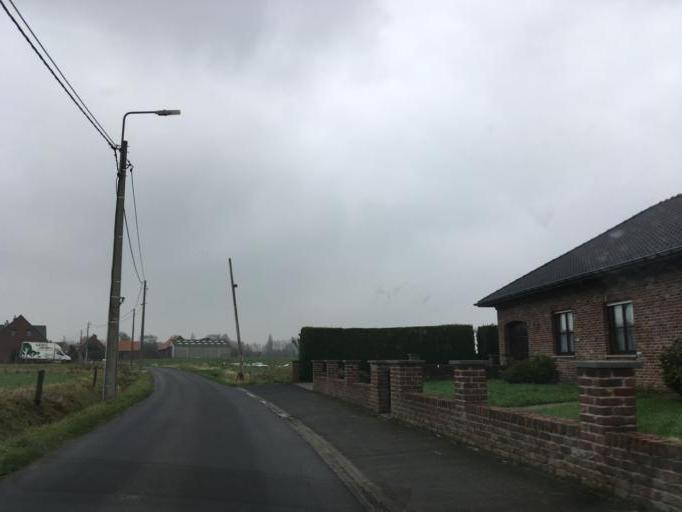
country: BE
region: Flanders
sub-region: Provincie West-Vlaanderen
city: Roeselare
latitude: 50.9772
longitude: 3.1378
